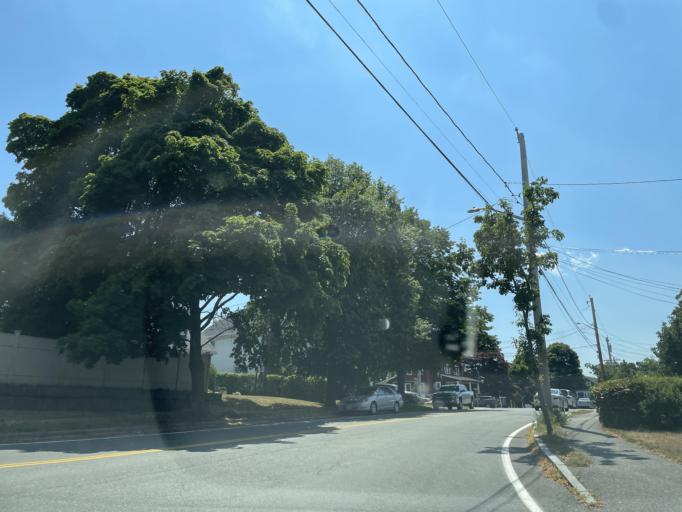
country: US
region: Massachusetts
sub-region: Norfolk County
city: Braintree
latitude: 42.2355
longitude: -71.0011
